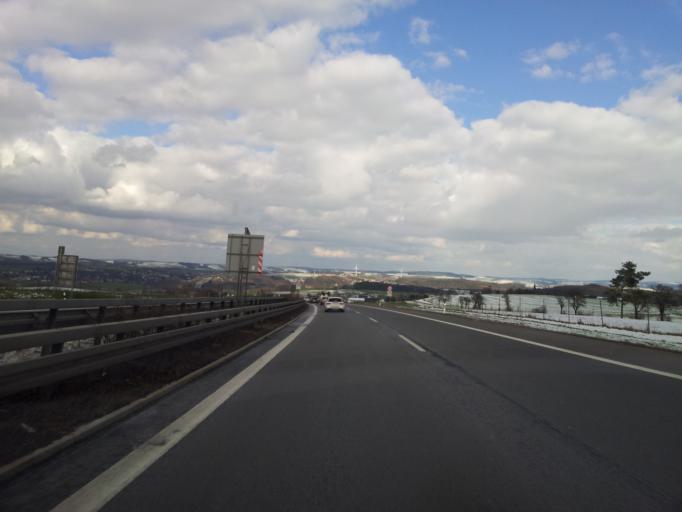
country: DE
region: Saxony
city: Wilkau-Hasslau
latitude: 50.6514
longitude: 12.4954
